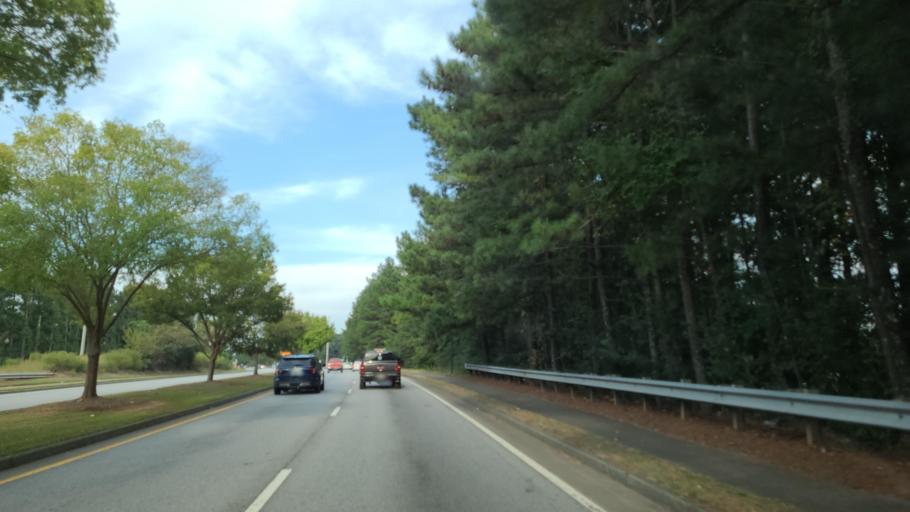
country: US
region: Georgia
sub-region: Cobb County
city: Smyrna
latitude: 33.8964
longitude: -84.5007
